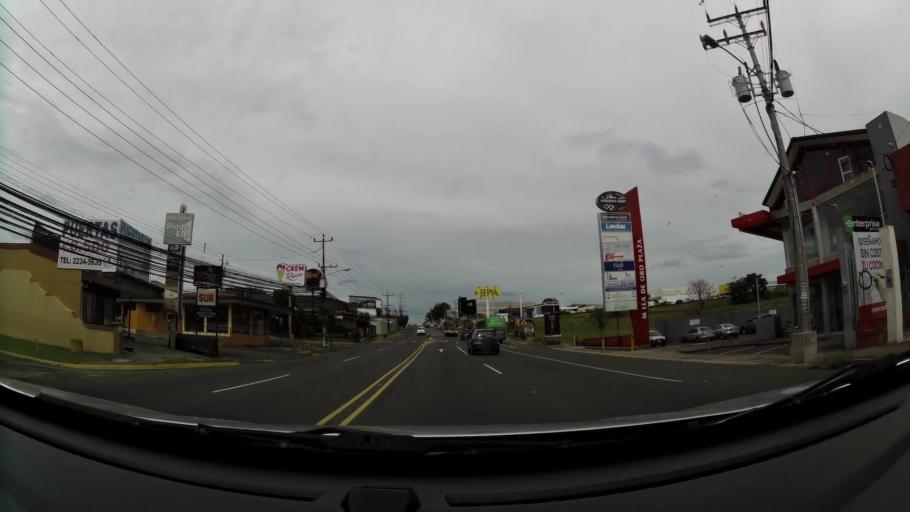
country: CR
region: San Jose
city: Curridabat
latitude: 9.9218
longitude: -84.0368
